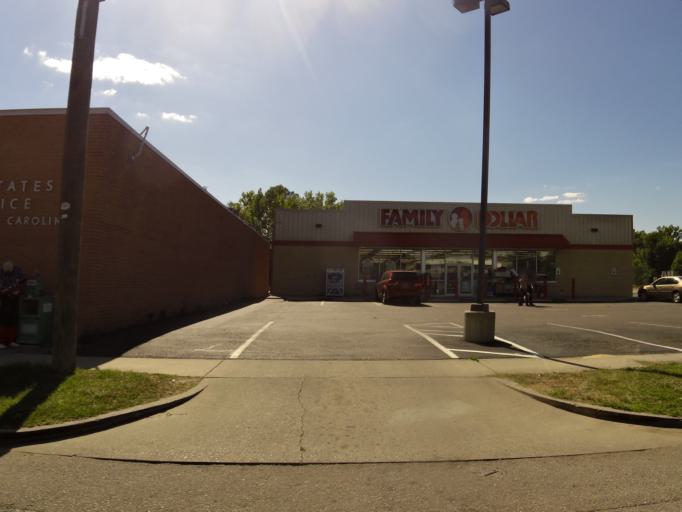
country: US
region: South Carolina
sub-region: Bamberg County
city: Denmark
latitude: 33.3219
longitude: -81.1427
